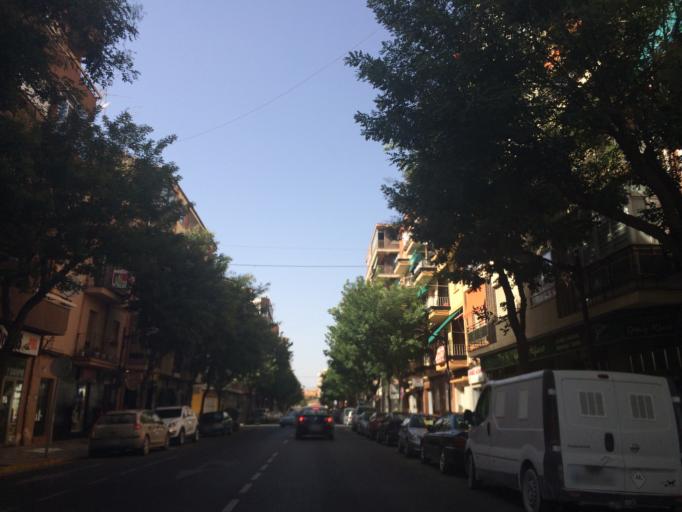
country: ES
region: Castille-La Mancha
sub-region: Provincia de Albacete
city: Albacete
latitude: 38.9942
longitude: -1.8671
